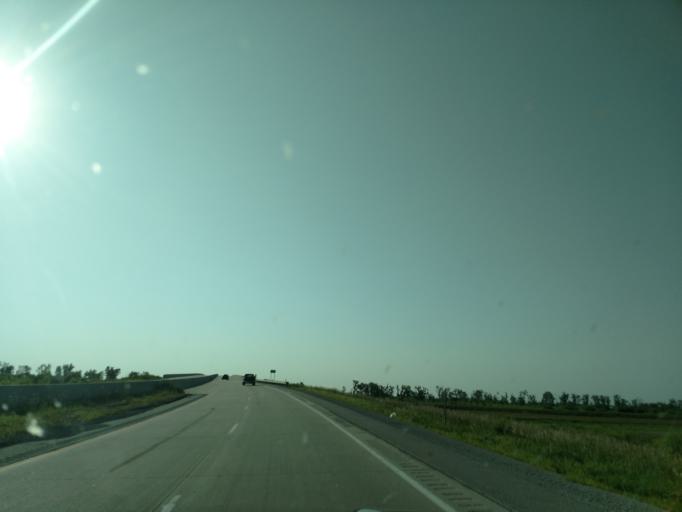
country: US
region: Nebraska
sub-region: Cass County
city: Plattsmouth
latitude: 41.0641
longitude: -95.8716
